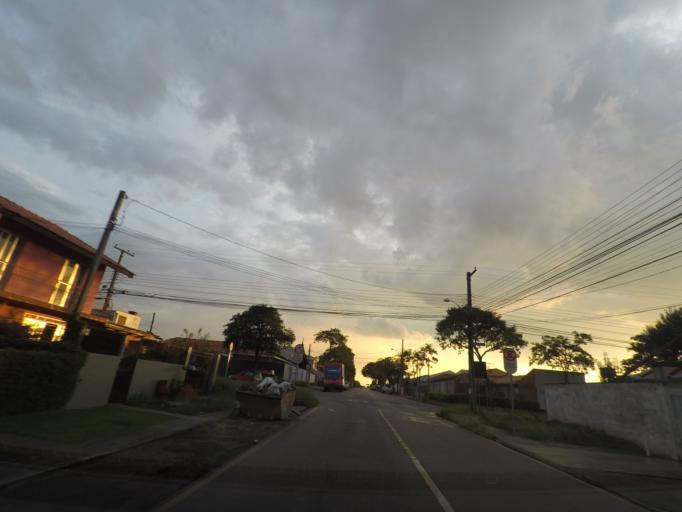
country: BR
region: Parana
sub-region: Sao Jose Dos Pinhais
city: Sao Jose dos Pinhais
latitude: -25.5025
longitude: -49.2517
